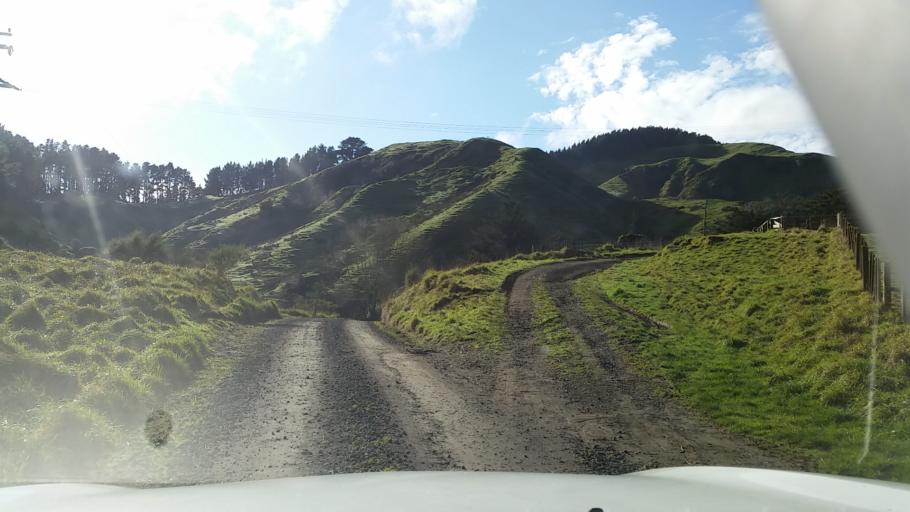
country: NZ
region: Taranaki
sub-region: South Taranaki District
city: Eltham
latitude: -39.5110
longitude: 174.3955
